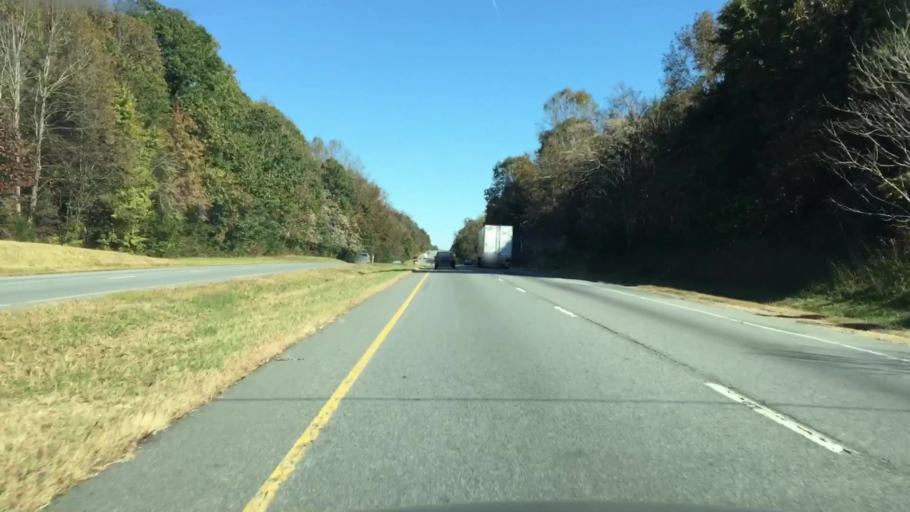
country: US
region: North Carolina
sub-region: Guilford County
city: McLeansville
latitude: 36.1877
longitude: -79.7046
